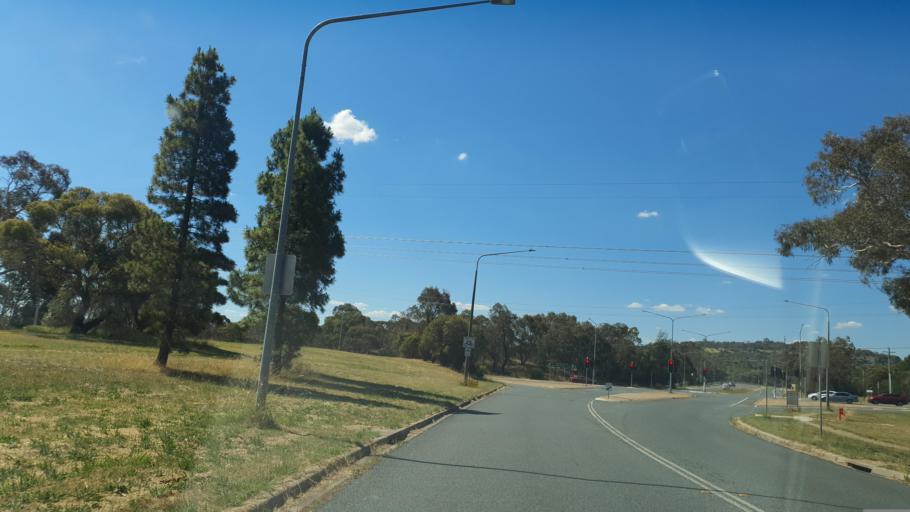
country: AU
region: Australian Capital Territory
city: Belconnen
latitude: -35.2209
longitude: 149.0541
